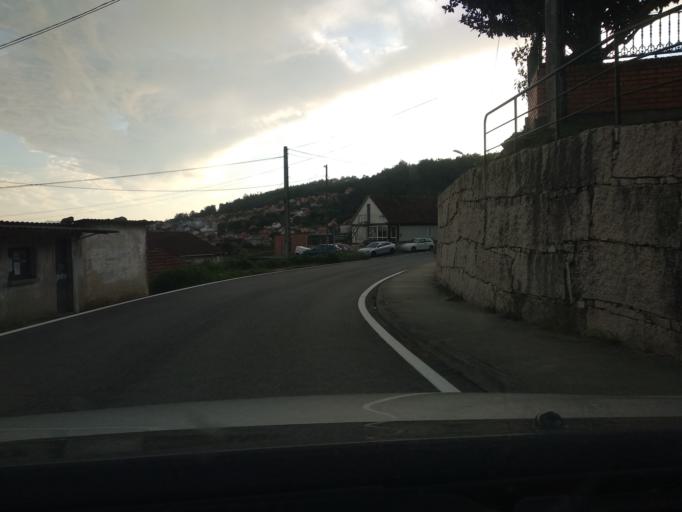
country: ES
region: Galicia
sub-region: Provincia de Pontevedra
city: Redondela
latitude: 42.2937
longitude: -8.6785
